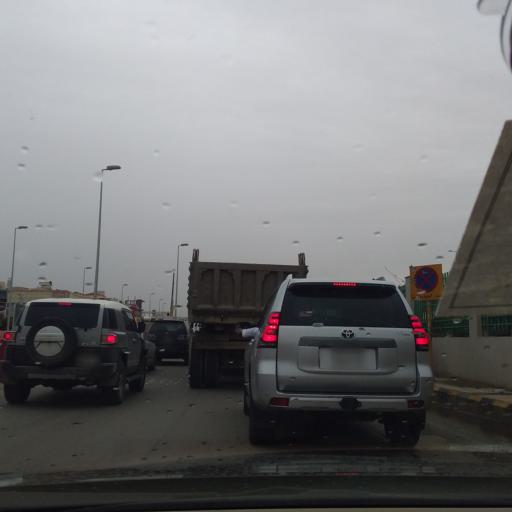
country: SA
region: Ar Riyad
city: Riyadh
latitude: 24.7320
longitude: 46.7859
